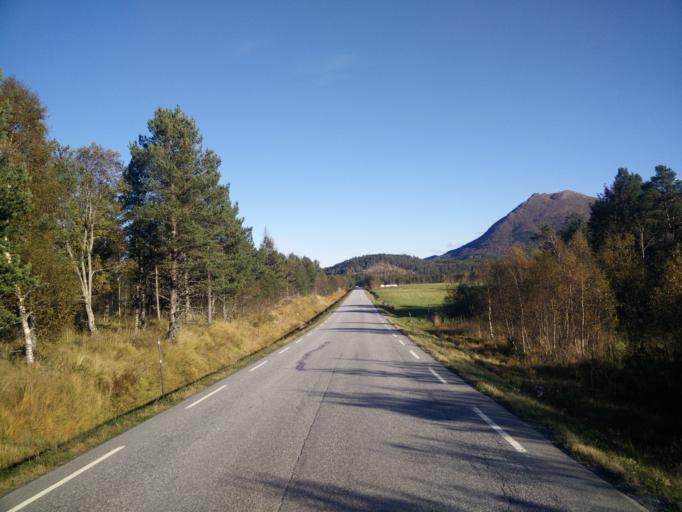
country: NO
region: More og Romsdal
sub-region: Halsa
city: Liaboen
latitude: 63.1250
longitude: 8.3583
